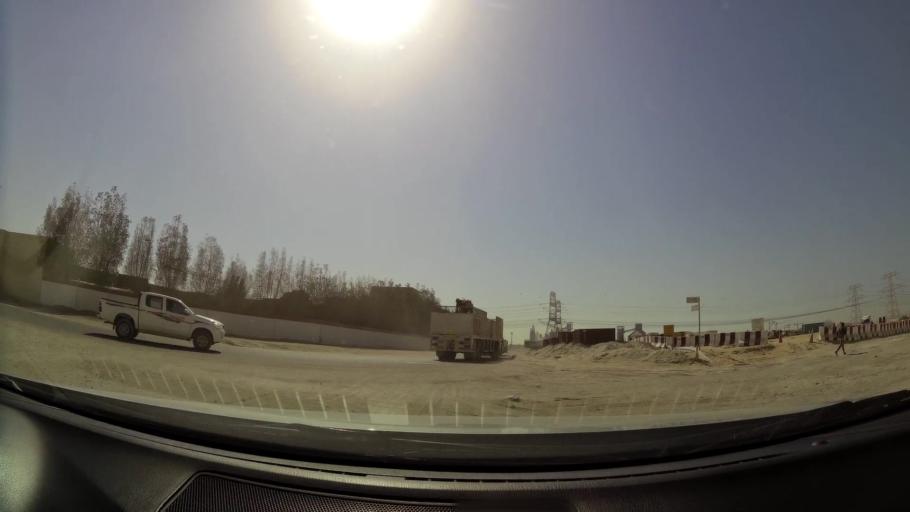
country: AE
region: Dubai
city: Dubai
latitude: 24.9973
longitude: 55.1413
